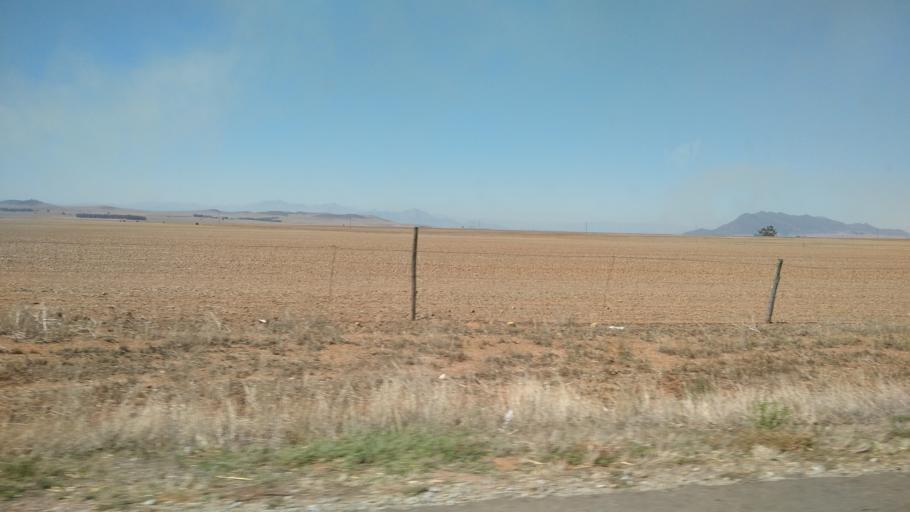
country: ZA
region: Western Cape
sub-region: West Coast District Municipality
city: Moorreesburg
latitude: -33.3137
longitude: 18.6217
